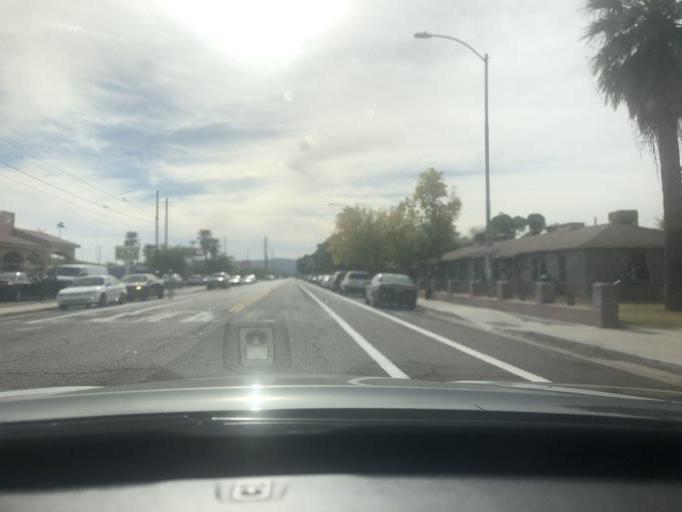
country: US
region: Arizona
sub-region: Maricopa County
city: Phoenix
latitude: 33.4555
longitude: -112.0389
